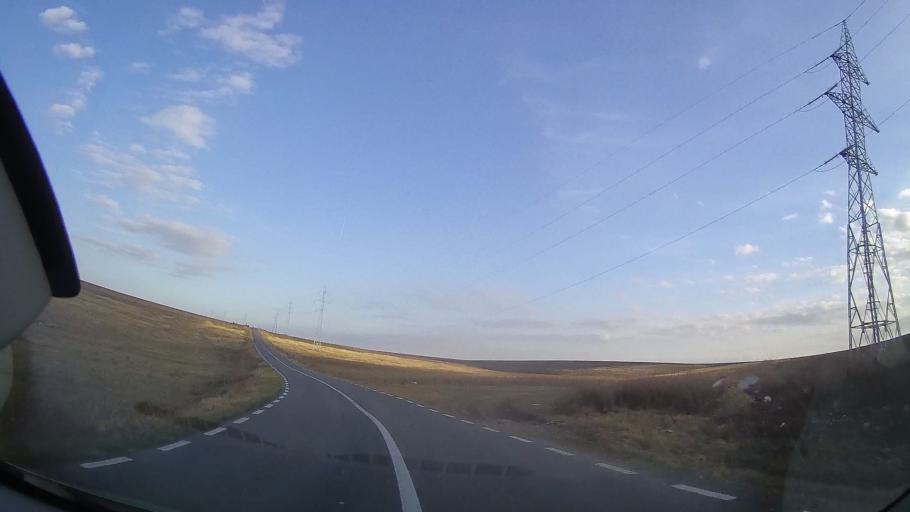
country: RO
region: Constanta
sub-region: Comuna Chirnogeni
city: Plopeni
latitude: 43.9542
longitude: 28.1510
